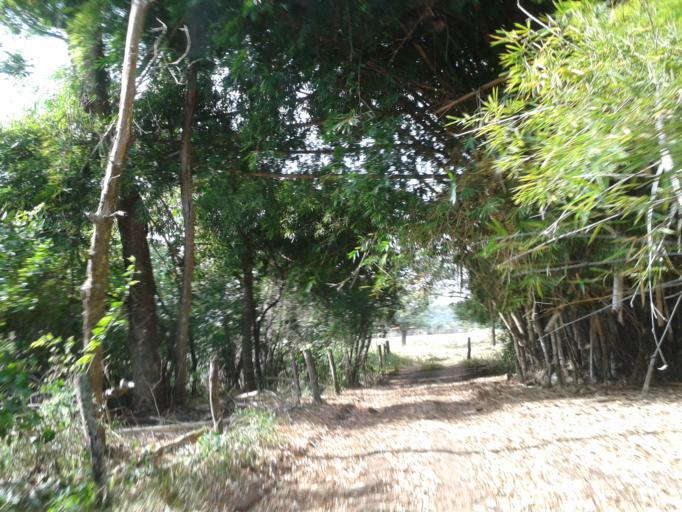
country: BR
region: Minas Gerais
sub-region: Campina Verde
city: Campina Verde
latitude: -19.4982
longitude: -49.5876
